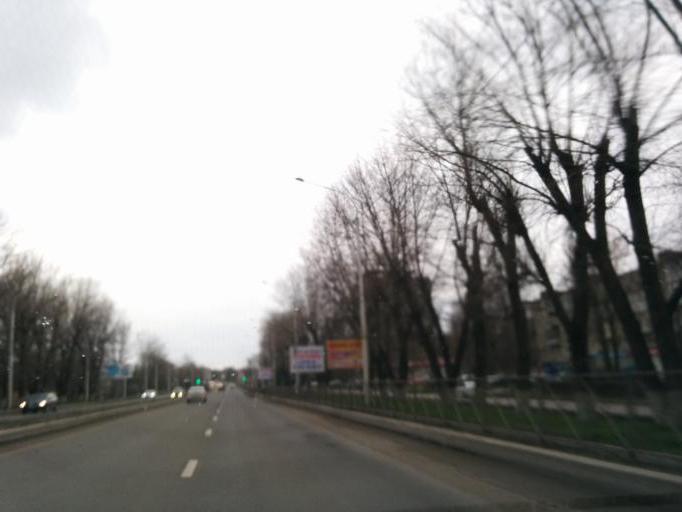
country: RU
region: Rostov
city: Novocherkassk
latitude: 47.4224
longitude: 40.0590
